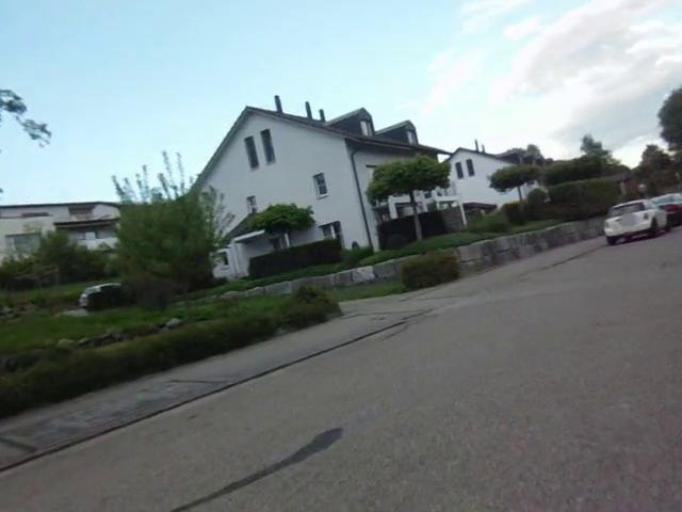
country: CH
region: Zurich
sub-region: Bezirk Hinwil
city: Rueti / Westlicher Dorfteil
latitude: 47.2519
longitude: 8.8471
